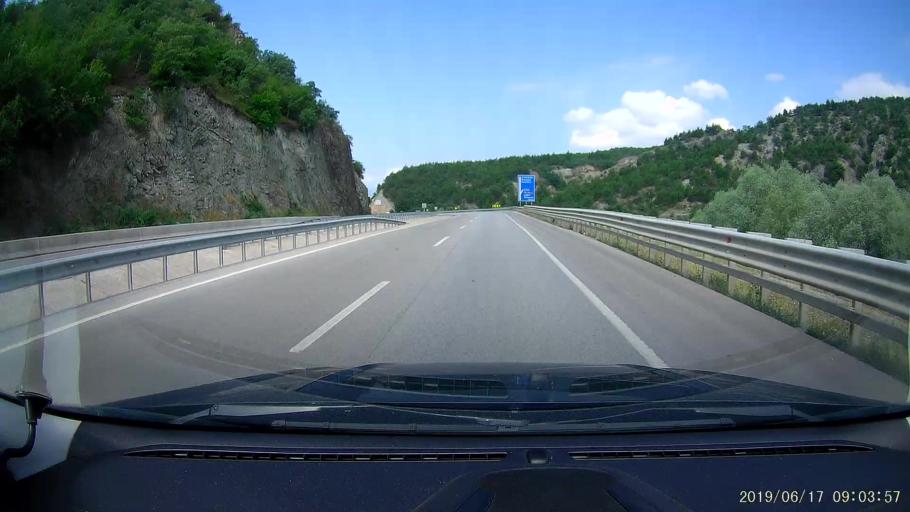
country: TR
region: Amasya
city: Tasova
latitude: 40.7486
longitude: 36.2980
